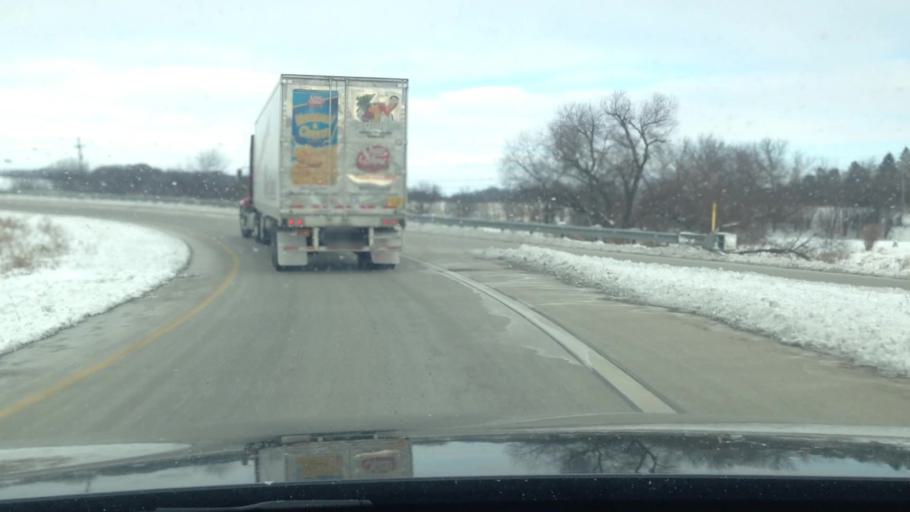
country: US
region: Wisconsin
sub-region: Walworth County
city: Lake Geneva
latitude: 42.5953
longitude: -88.4068
